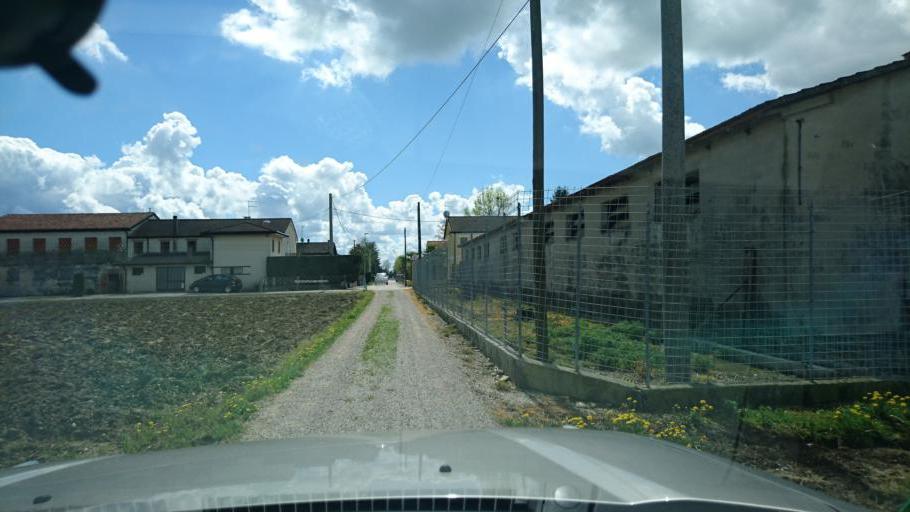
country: IT
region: Veneto
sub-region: Provincia di Padova
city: Piazzola sul Brenta
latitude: 45.5447
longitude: 11.7666
